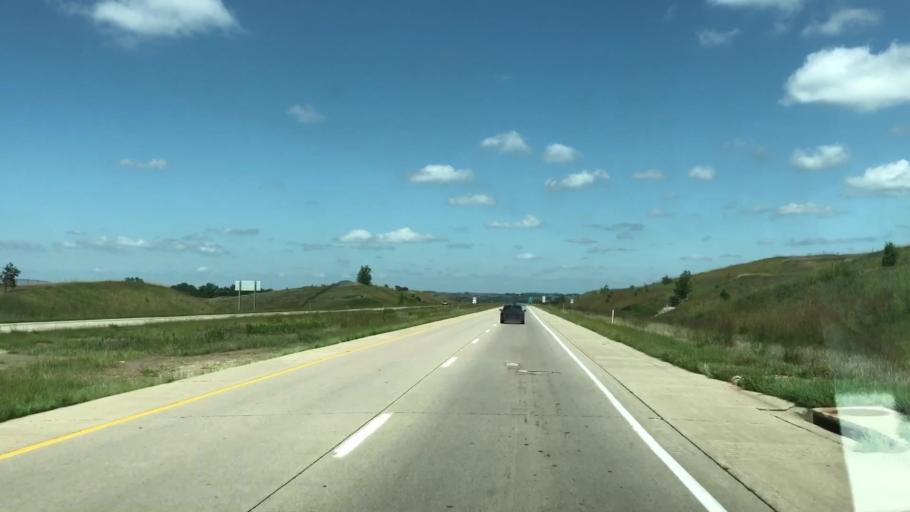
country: US
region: Iowa
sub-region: Woodbury County
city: Sioux City
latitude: 42.5255
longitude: -96.3389
